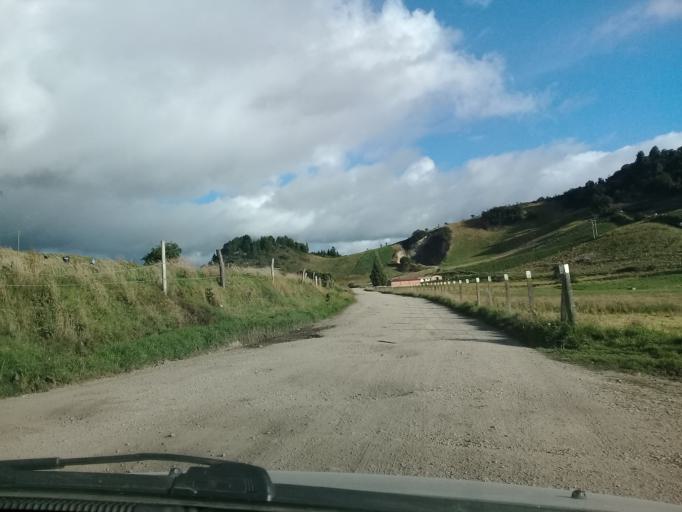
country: CO
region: Cundinamarca
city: Villapinzon
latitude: 5.2436
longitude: -73.6624
